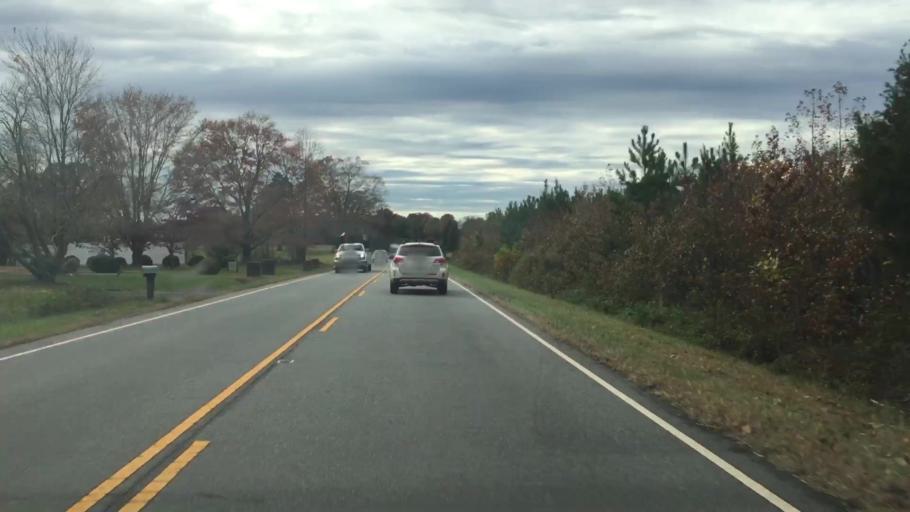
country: US
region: North Carolina
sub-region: Guilford County
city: Summerfield
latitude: 36.2756
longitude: -79.7980
